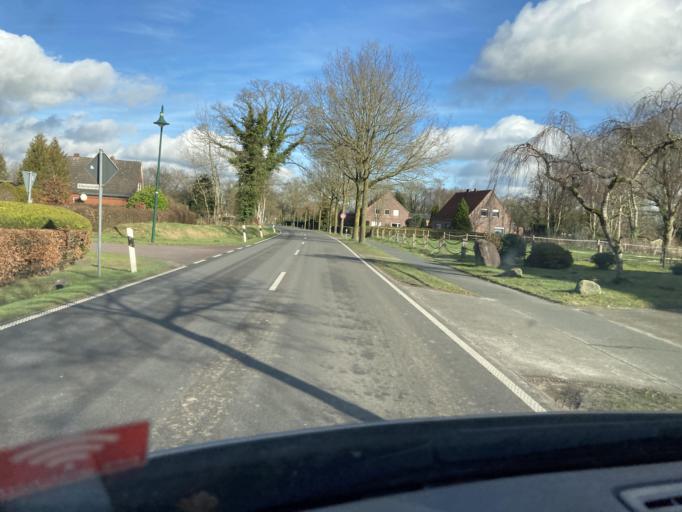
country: DE
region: Lower Saxony
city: Schwerinsdorf
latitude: 53.2842
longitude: 7.7291
